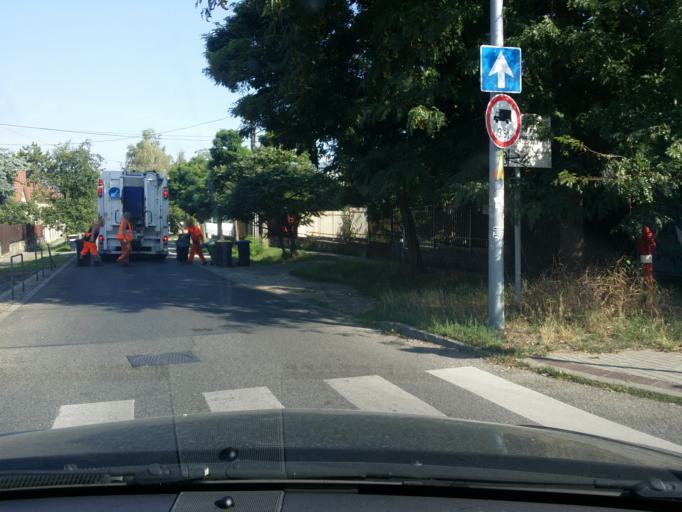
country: HU
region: Budapest
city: Budapest XVI. keruelet
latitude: 47.5261
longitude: 19.1624
